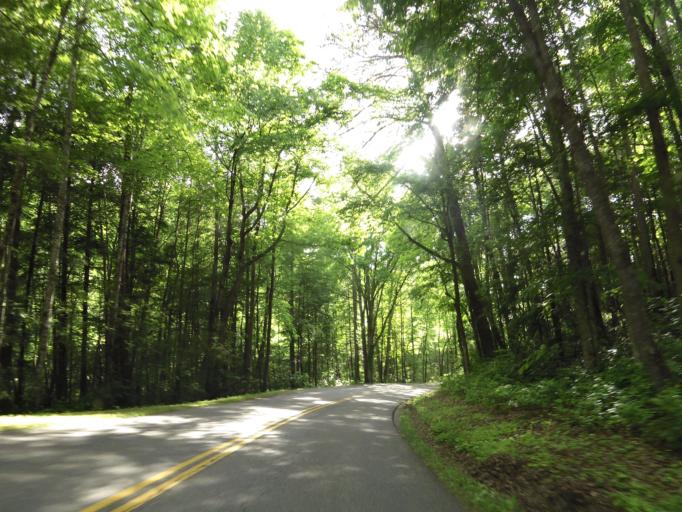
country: US
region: Tennessee
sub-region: Sevier County
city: Gatlinburg
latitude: 35.6627
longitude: -83.6160
